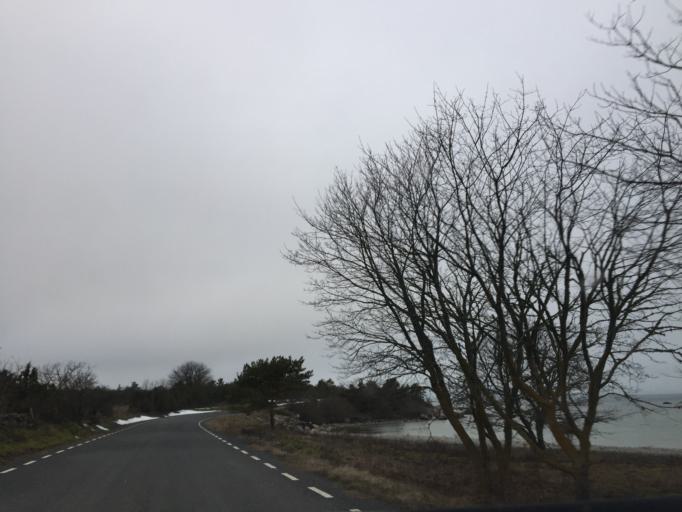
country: EE
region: Saare
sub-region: Kuressaare linn
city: Kuressaare
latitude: 58.5647
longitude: 22.3120
